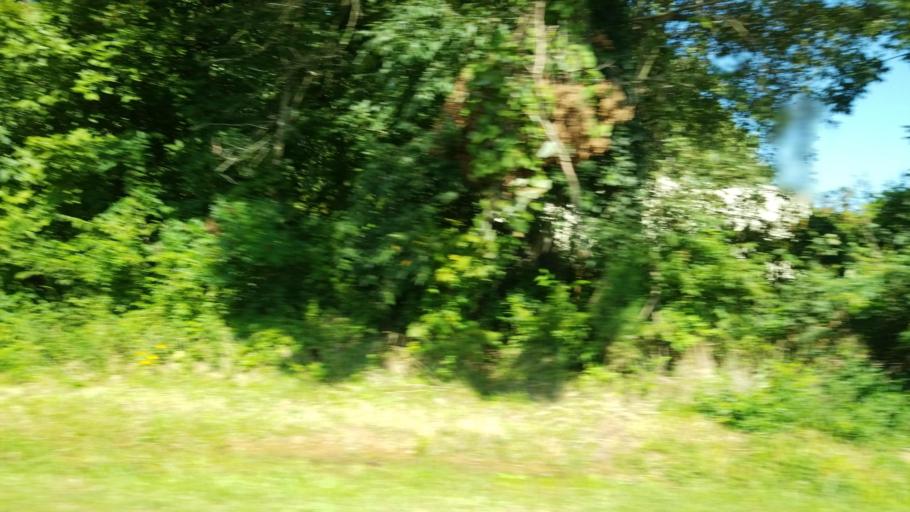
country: US
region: Illinois
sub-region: Saline County
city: Carrier Mills
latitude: 37.8013
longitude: -88.7164
